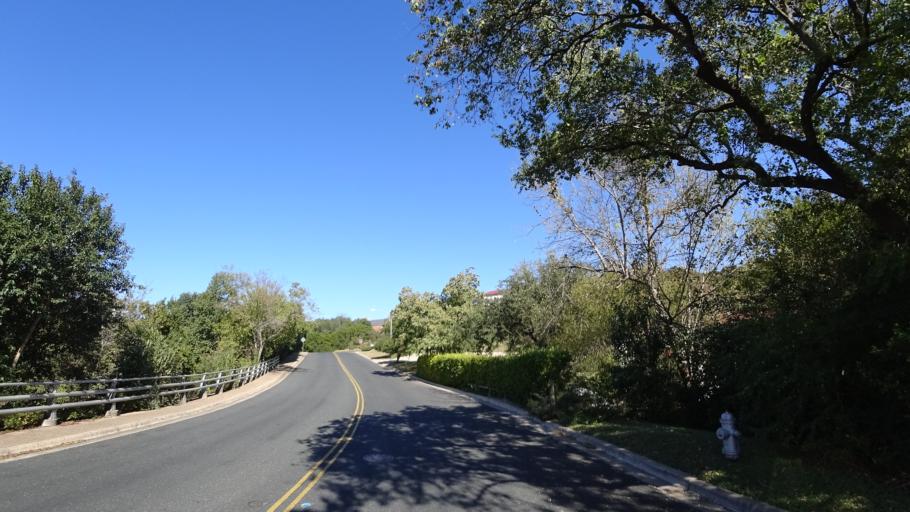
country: US
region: Texas
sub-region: Williamson County
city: Jollyville
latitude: 30.4058
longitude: -97.7504
